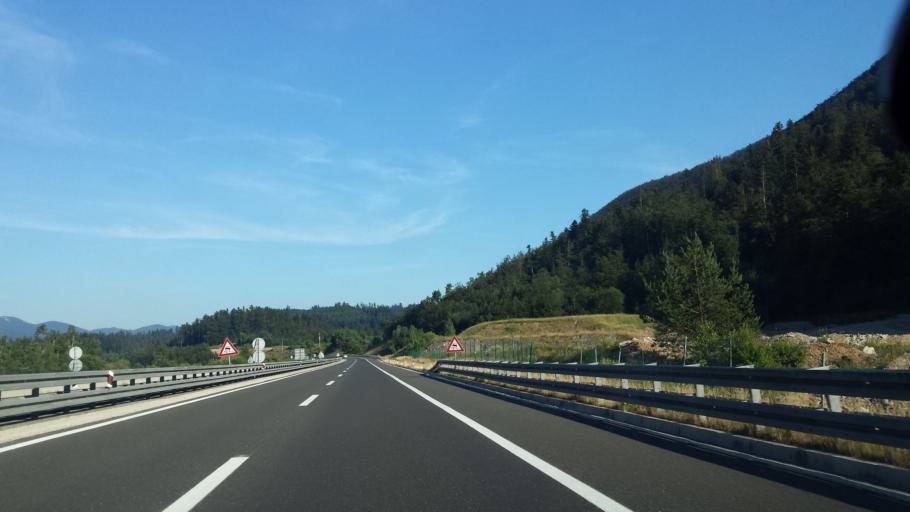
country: HR
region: Primorsko-Goranska
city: Hreljin
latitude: 45.3232
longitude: 14.6613
